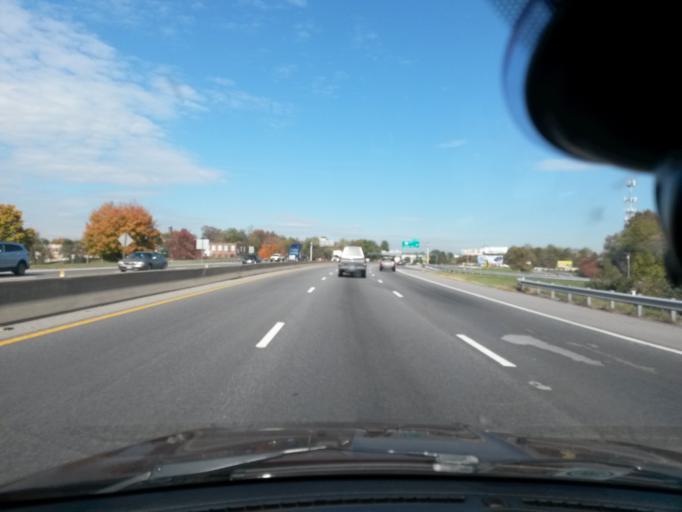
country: US
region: Virginia
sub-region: City of Roanoke
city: Roanoke
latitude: 37.2808
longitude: -79.9380
